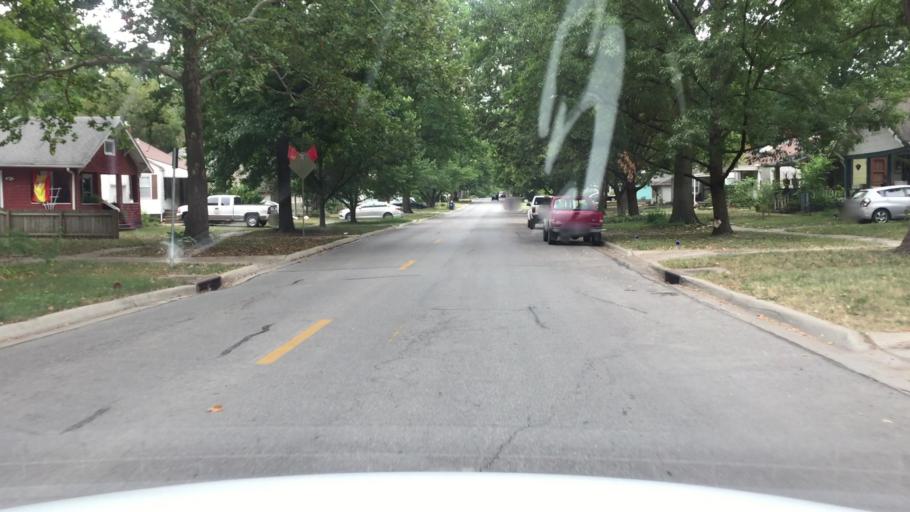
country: US
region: Kansas
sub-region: Douglas County
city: Lawrence
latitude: 38.9463
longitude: -95.2394
